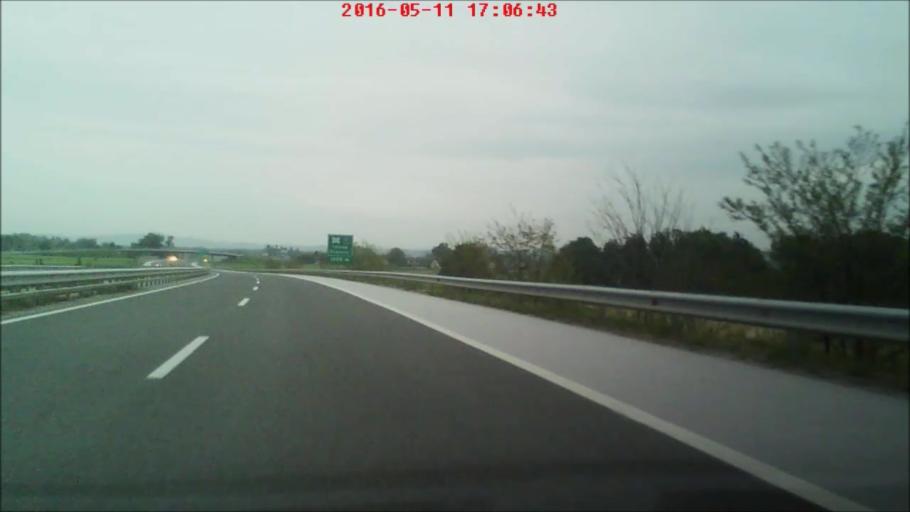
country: SI
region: Hajdina
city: Spodnja Hajdina
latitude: 46.4003
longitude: 15.8325
